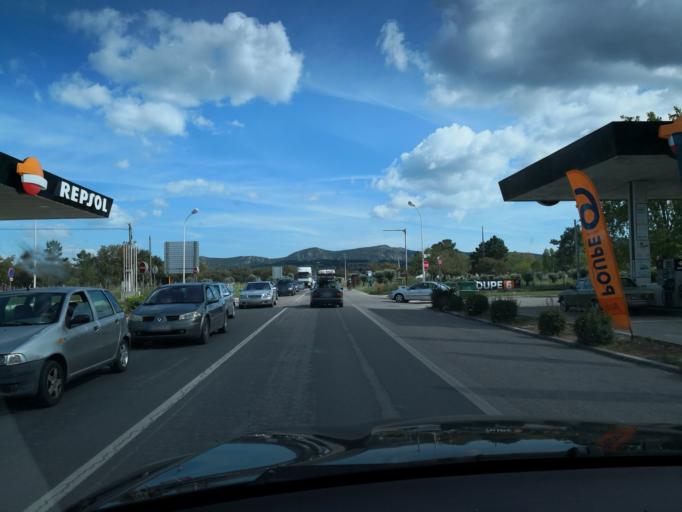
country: PT
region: Setubal
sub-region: Palmela
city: Quinta do Anjo
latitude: 38.5307
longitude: -9.0209
